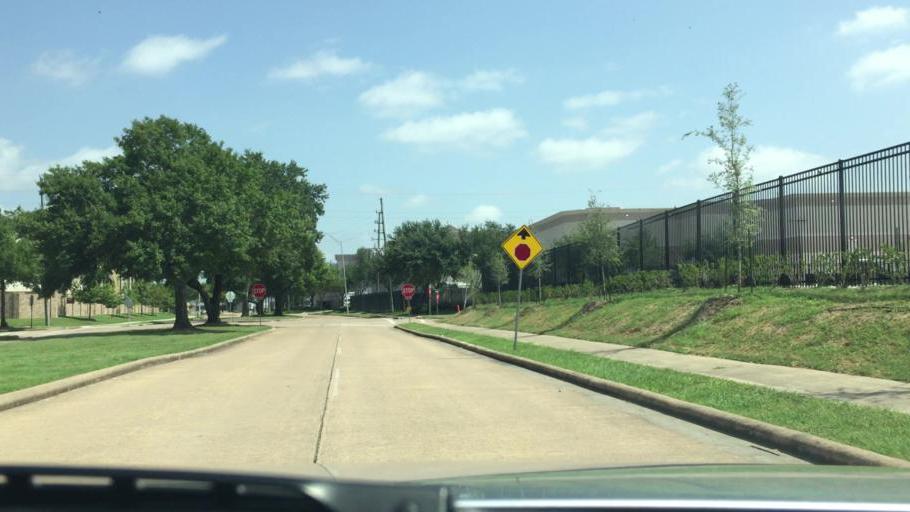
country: US
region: Texas
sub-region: Harris County
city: Bunker Hill Village
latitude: 29.7330
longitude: -95.5953
